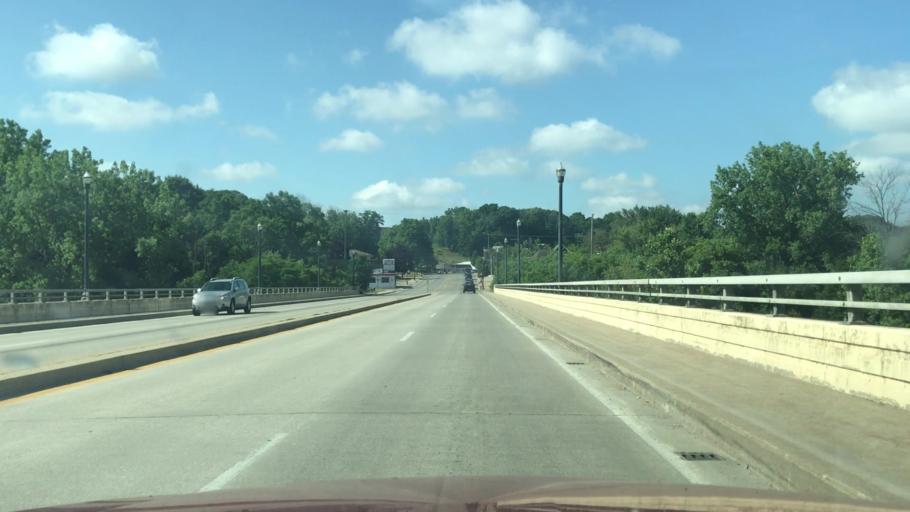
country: US
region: Michigan
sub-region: Newaygo County
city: Newaygo
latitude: 43.4232
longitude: -85.7982
